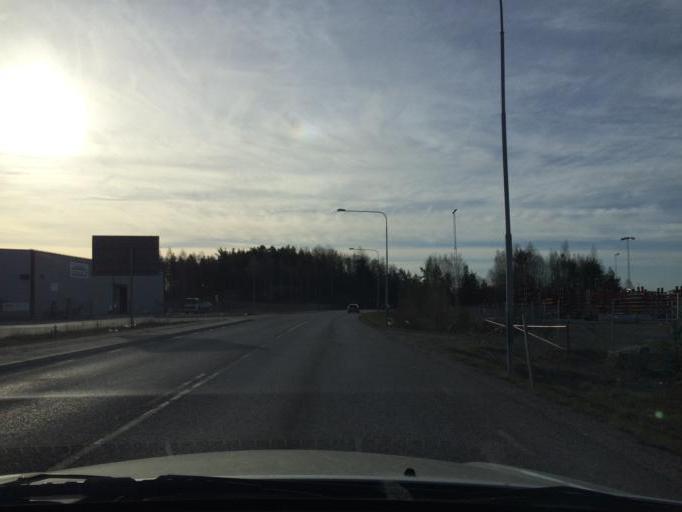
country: SE
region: Soedermanland
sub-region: Eskilstuna Kommun
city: Hallbybrunn
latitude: 59.4010
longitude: 16.4271
